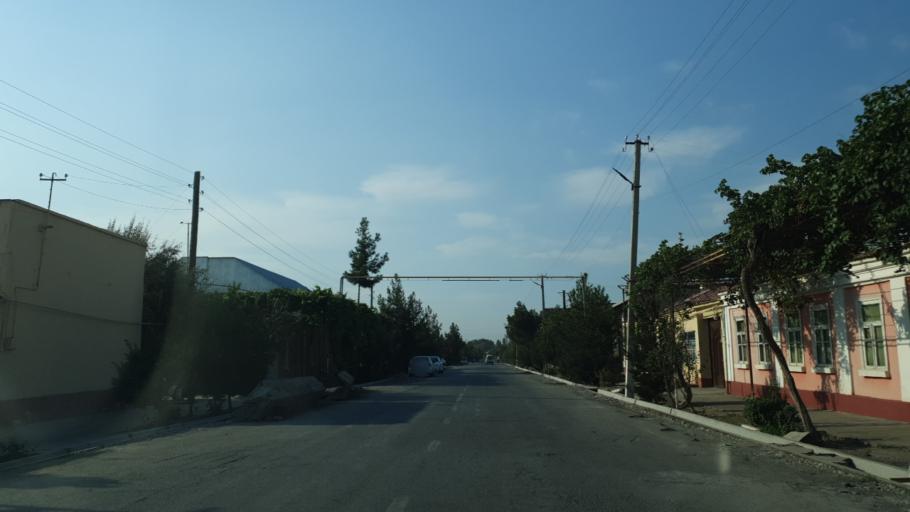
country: UZ
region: Fergana
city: Yaypan
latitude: 40.3713
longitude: 70.8134
